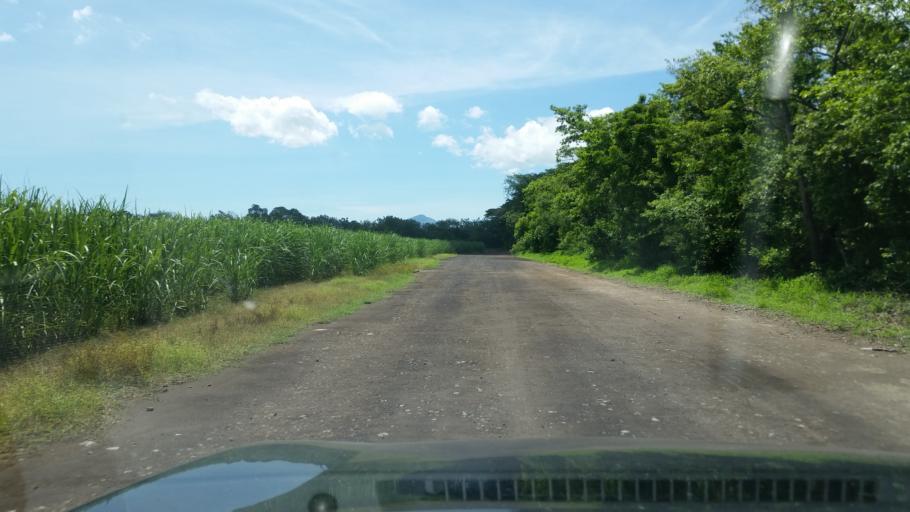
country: NI
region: Chinandega
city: El Viejo
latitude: 12.7460
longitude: -87.1368
